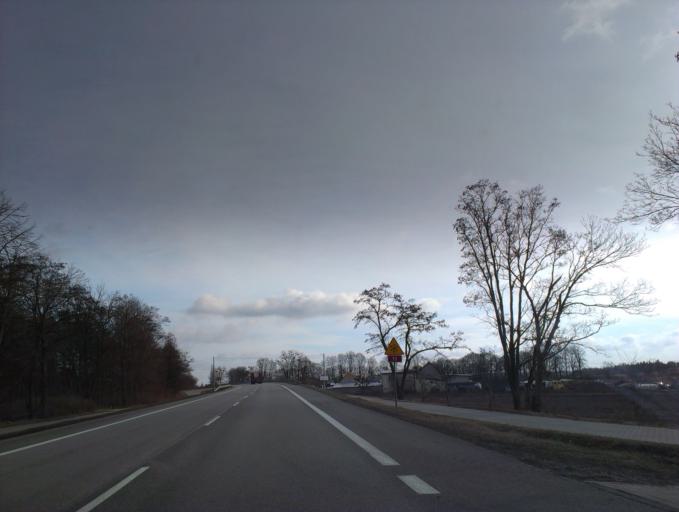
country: PL
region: Kujawsko-Pomorskie
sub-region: Powiat lipnowski
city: Lipno
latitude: 52.8564
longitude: 19.1607
